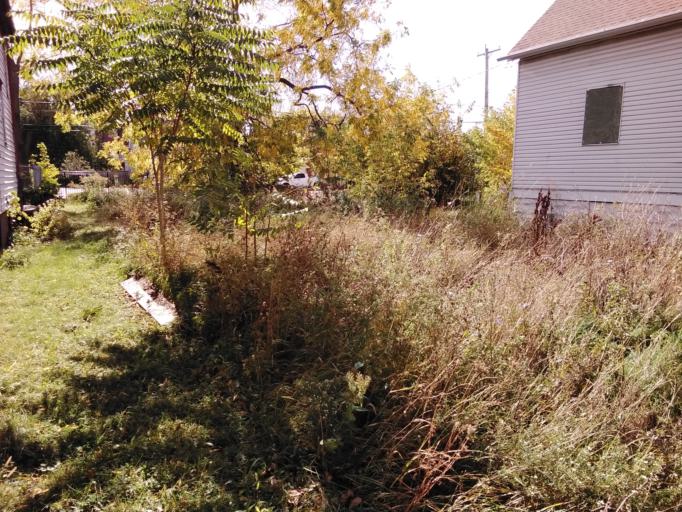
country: US
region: Wisconsin
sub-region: Milwaukee County
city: Milwaukee
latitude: 43.0660
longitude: -87.9496
